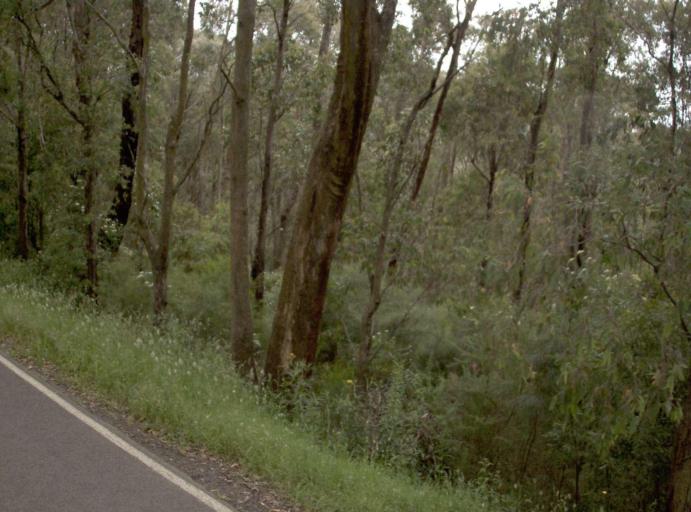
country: AU
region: Victoria
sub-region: Latrobe
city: Moe
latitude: -37.9394
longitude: 146.1144
